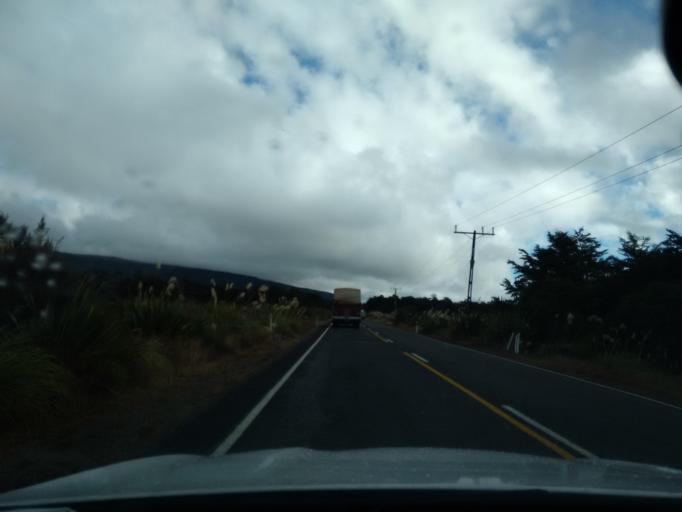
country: NZ
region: Manawatu-Wanganui
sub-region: Ruapehu District
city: Waiouru
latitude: -39.1714
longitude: 175.4777
